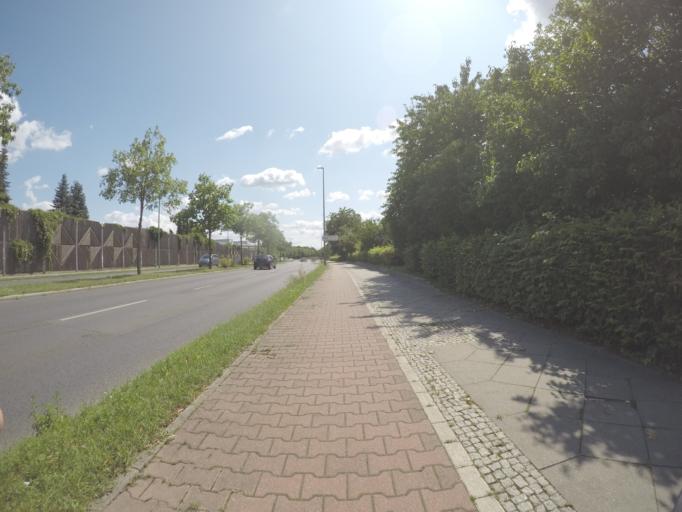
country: DE
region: Berlin
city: Marzahn
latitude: 52.5304
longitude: 13.5654
